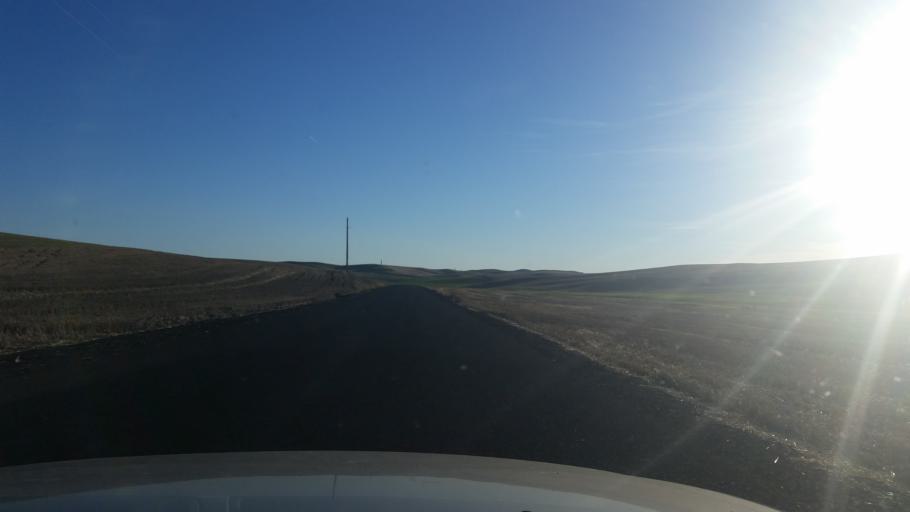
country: US
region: Washington
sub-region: Spokane County
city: Cheney
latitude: 47.3509
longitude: -117.4507
